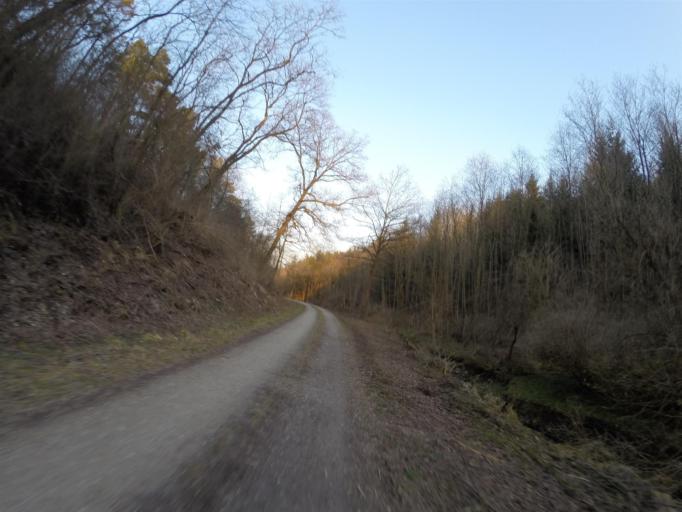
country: DE
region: Thuringia
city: Grossschwabhausen
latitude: 50.9453
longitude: 11.5186
